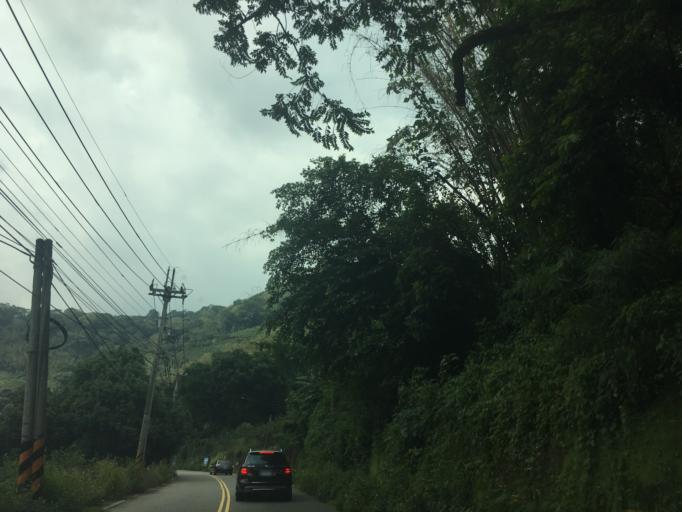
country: TW
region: Taiwan
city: Fengyuan
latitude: 24.3172
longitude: 120.9236
